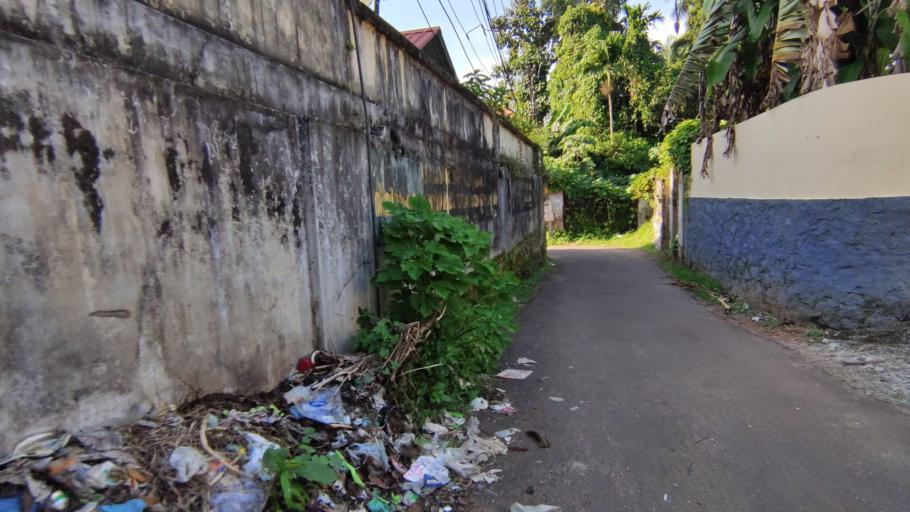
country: IN
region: Kerala
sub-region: Kottayam
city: Kottayam
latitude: 9.5966
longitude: 76.5120
